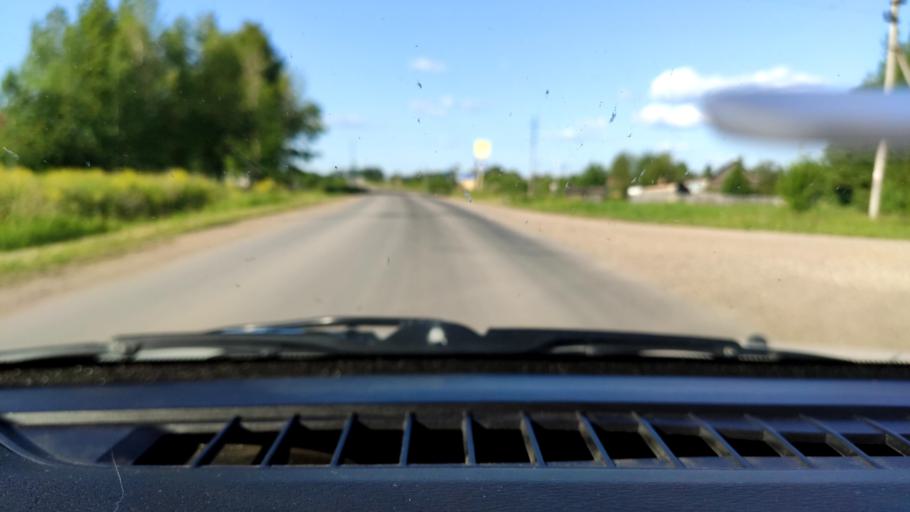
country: RU
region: Perm
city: Uinskoye
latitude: 57.0935
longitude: 56.6389
